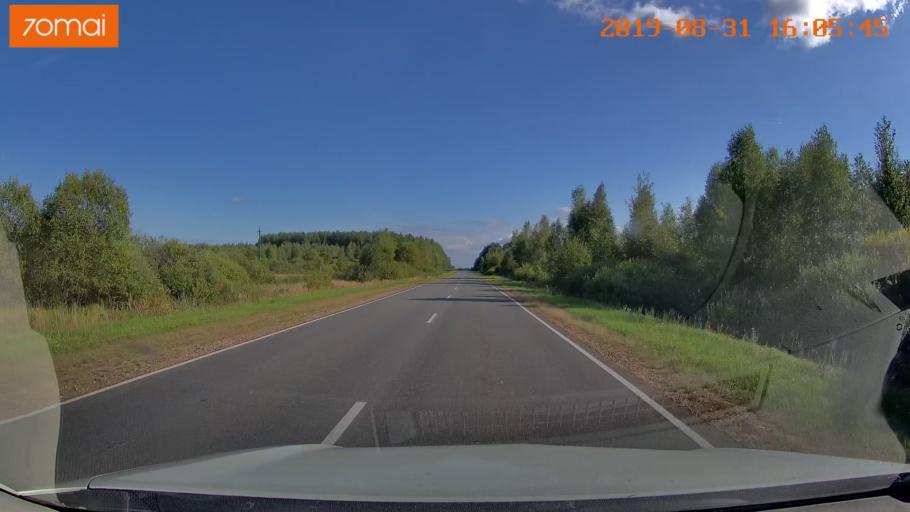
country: RU
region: Kaluga
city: Yukhnov
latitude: 54.6343
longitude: 35.3381
